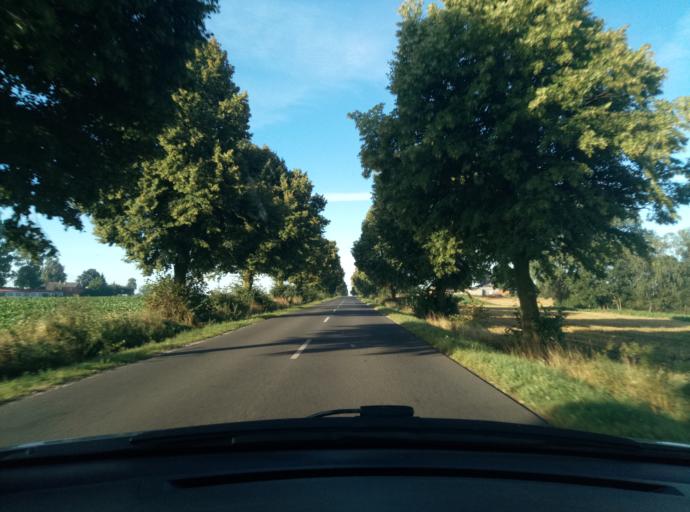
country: PL
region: Kujawsko-Pomorskie
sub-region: Powiat golubsko-dobrzynski
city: Kowalewo Pomorskie
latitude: 53.2100
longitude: 18.9248
